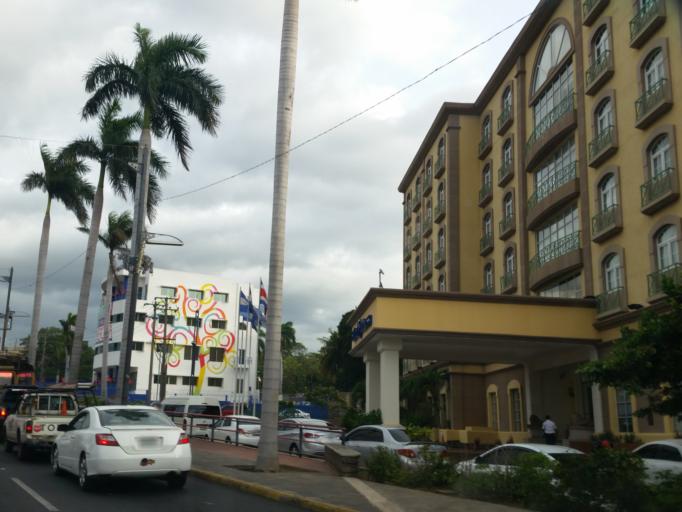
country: NI
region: Managua
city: Managua
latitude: 12.1240
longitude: -86.2646
